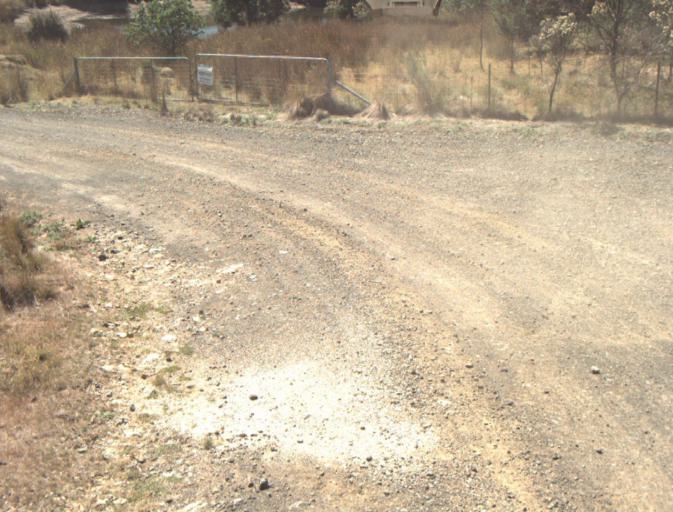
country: AU
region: Tasmania
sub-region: Dorset
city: Scottsdale
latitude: -41.3187
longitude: 147.3844
